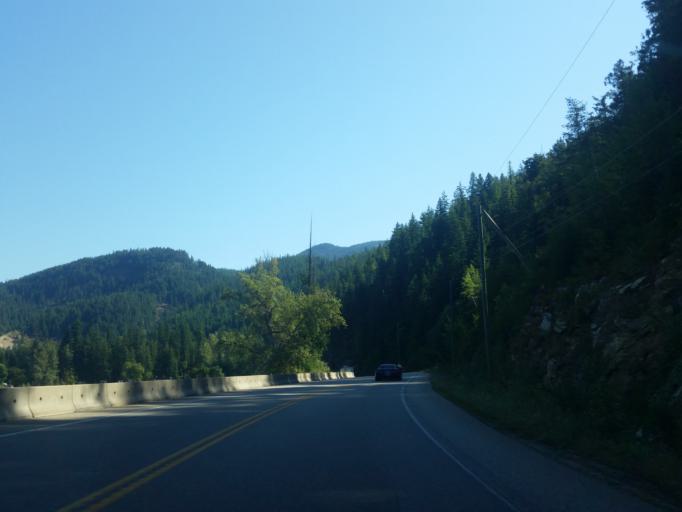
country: CA
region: British Columbia
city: Sicamous
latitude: 50.8004
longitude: -118.9778
